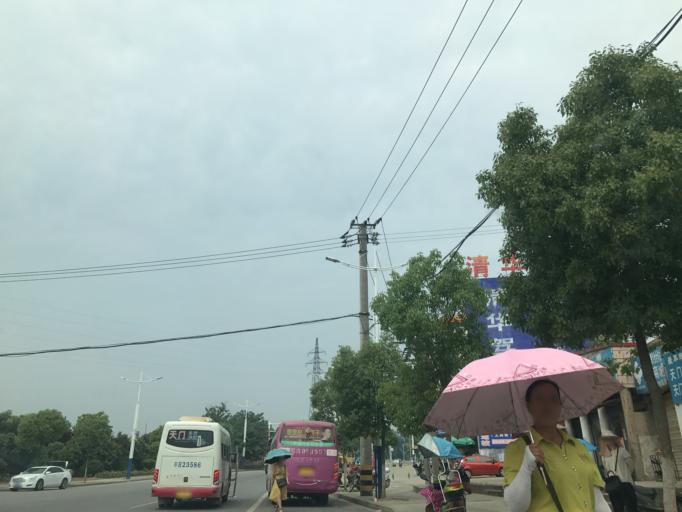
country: CN
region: Hubei
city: Tianmen
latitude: 30.6607
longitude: 113.1340
